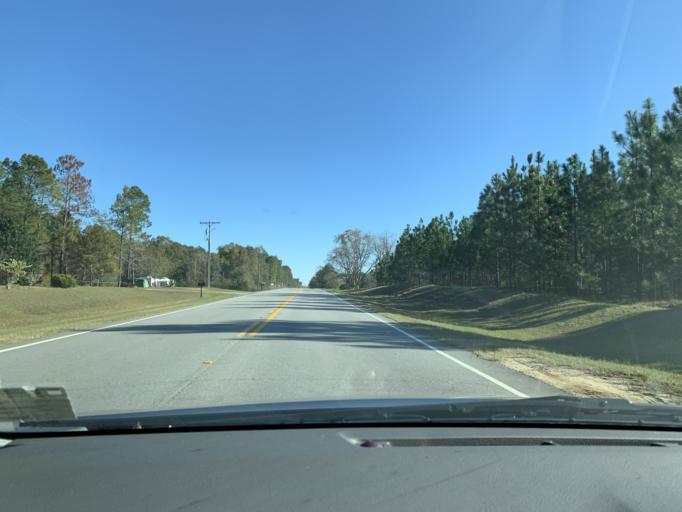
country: US
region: Georgia
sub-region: Ben Hill County
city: Fitzgerald
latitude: 31.7345
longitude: -83.1667
